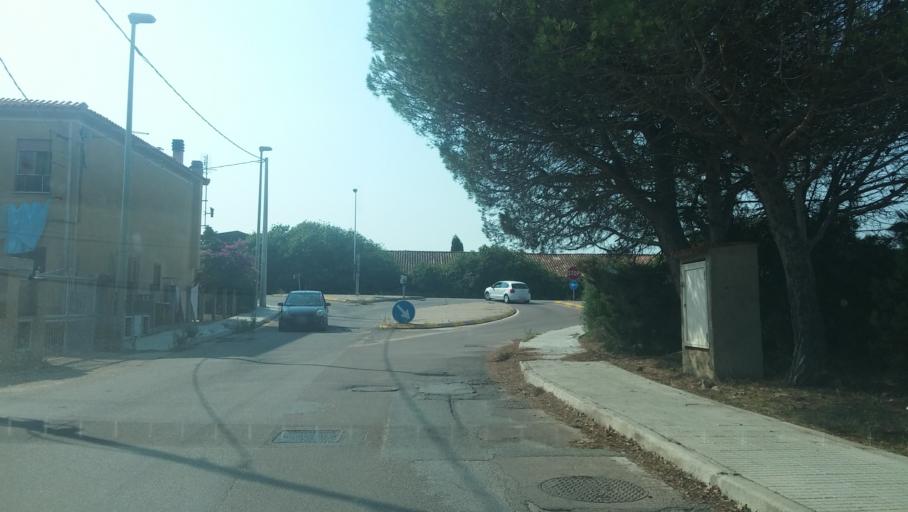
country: IT
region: Sardinia
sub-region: Provincia di Olbia-Tempio
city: La Maddalena
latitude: 41.2204
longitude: 9.4357
